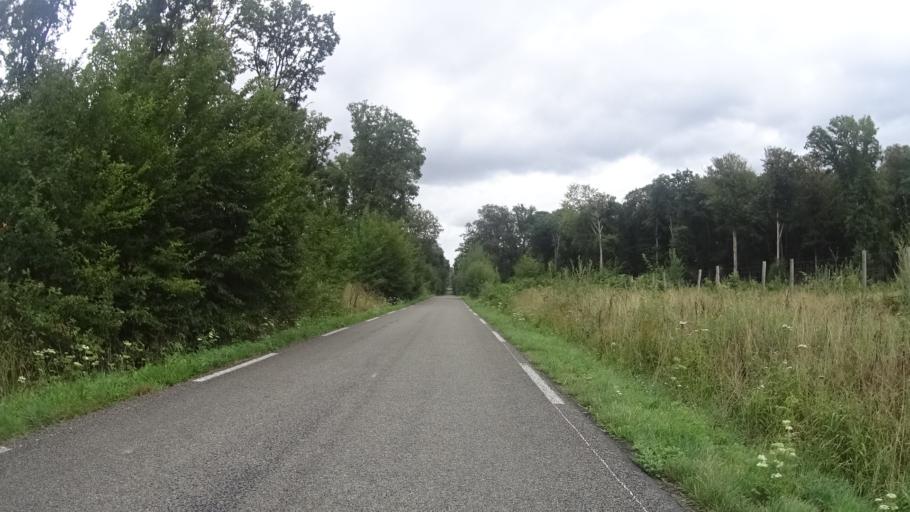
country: FR
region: Nord-Pas-de-Calais
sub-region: Departement du Nord
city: Maroilles
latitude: 50.1648
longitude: 3.7680
